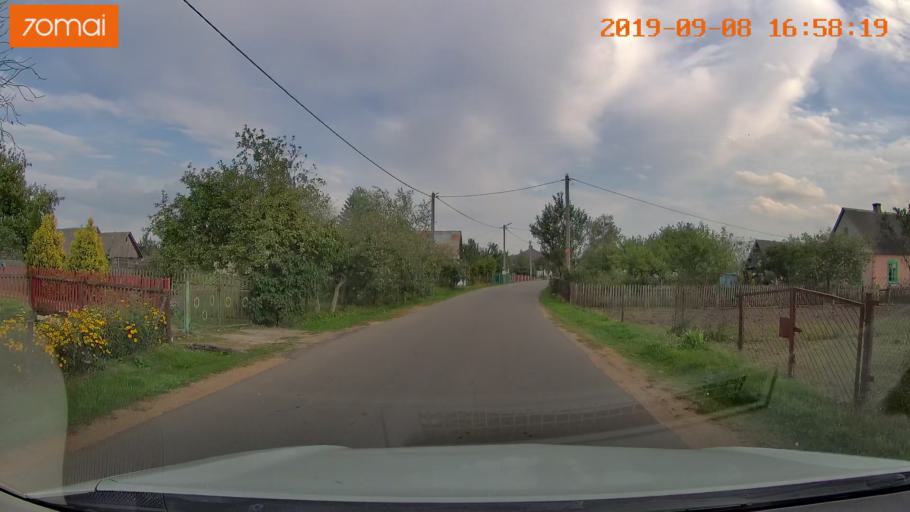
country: BY
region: Grodnenskaya
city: Hrodna
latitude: 53.7275
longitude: 23.9260
